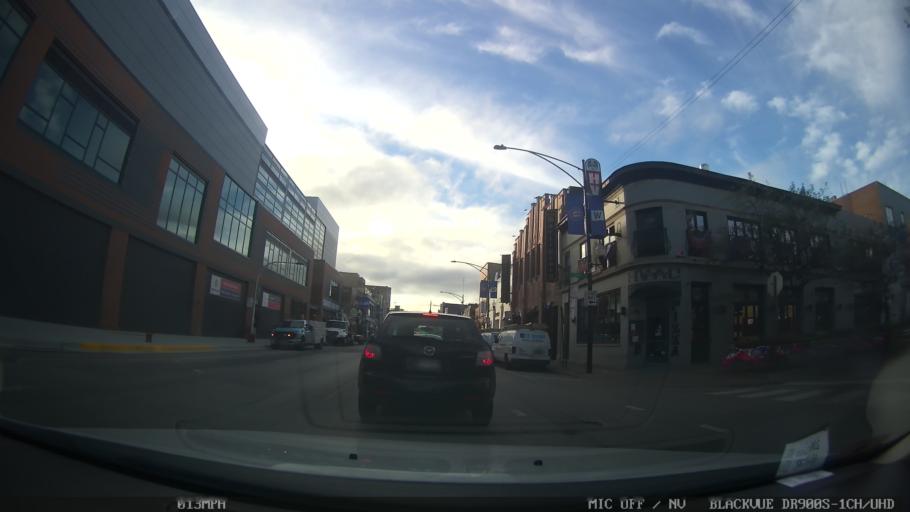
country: US
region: Illinois
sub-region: Cook County
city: Lincolnwood
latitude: 41.9465
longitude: -87.6560
